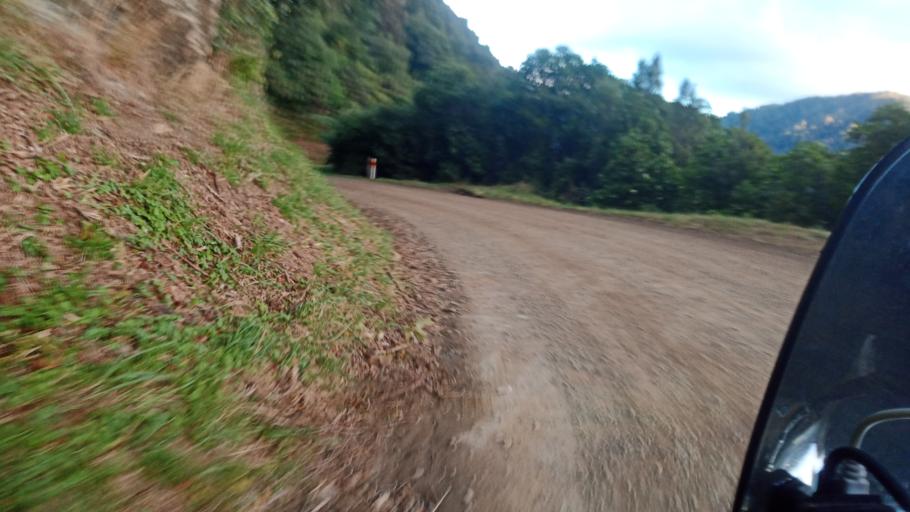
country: NZ
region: Hawke's Bay
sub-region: Wairoa District
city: Wairoa
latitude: -38.7243
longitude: 177.0653
